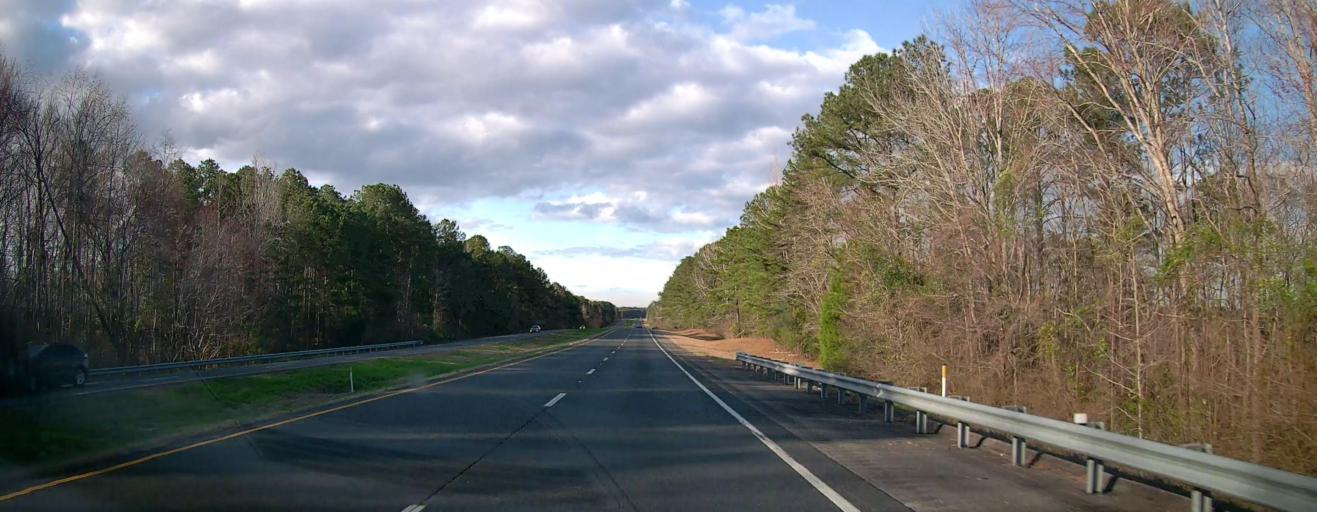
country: US
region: Georgia
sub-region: Harris County
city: Hamilton
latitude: 32.5901
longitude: -84.8208
